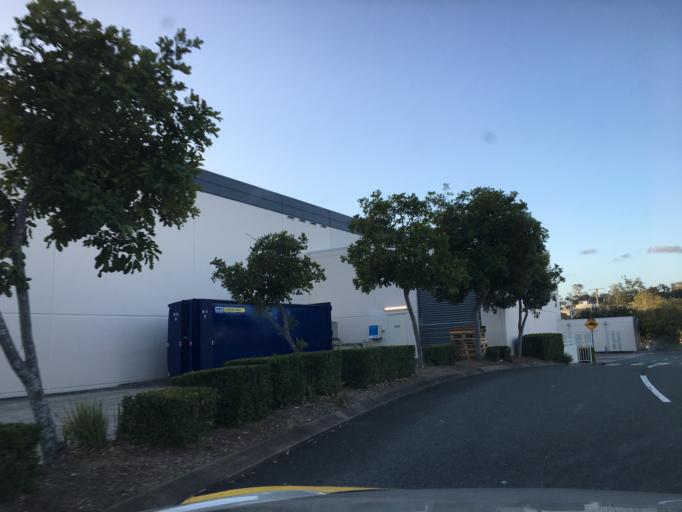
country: AU
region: Queensland
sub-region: Logan
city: Slacks Creek
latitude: -27.6569
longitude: 153.1720
